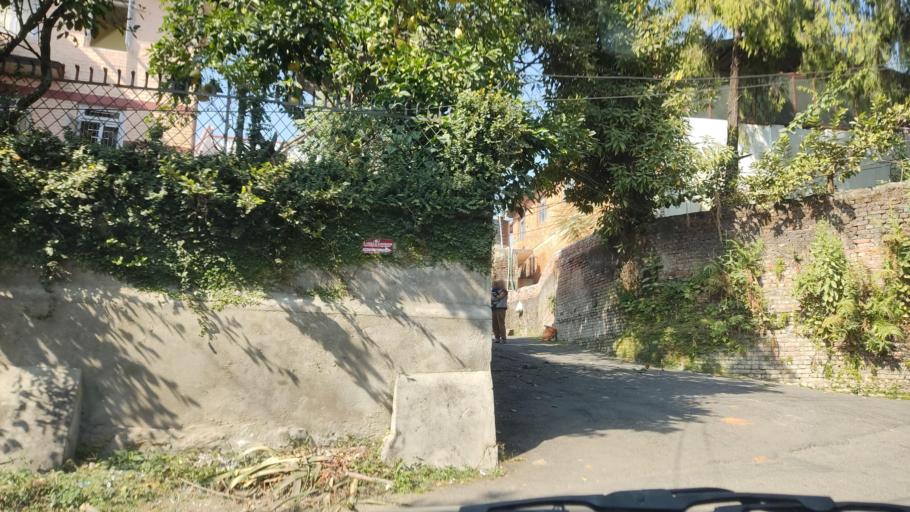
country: NP
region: Central Region
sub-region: Bagmati Zone
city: Kathmandu
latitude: 27.7244
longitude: 85.3362
